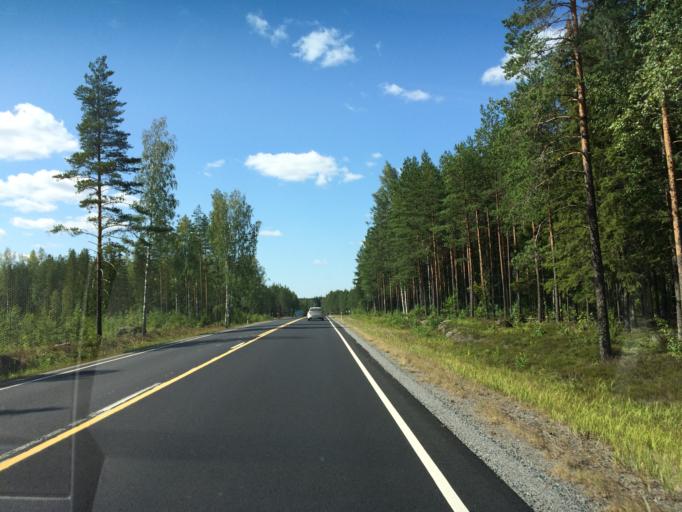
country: FI
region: Pirkanmaa
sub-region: Lounais-Pirkanmaa
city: Kiikoinen
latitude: 61.4751
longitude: 22.4729
